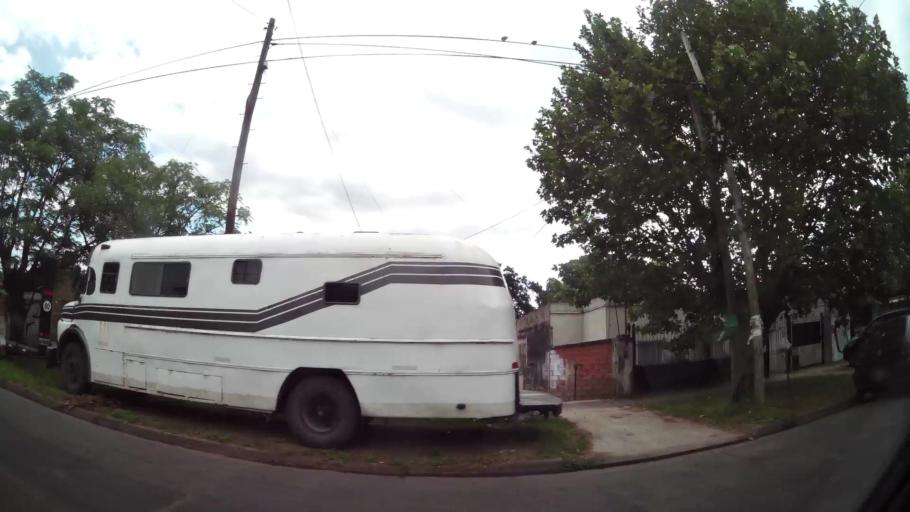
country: AR
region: Buenos Aires
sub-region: Partido de Tigre
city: Tigre
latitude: -34.4698
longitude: -58.6479
